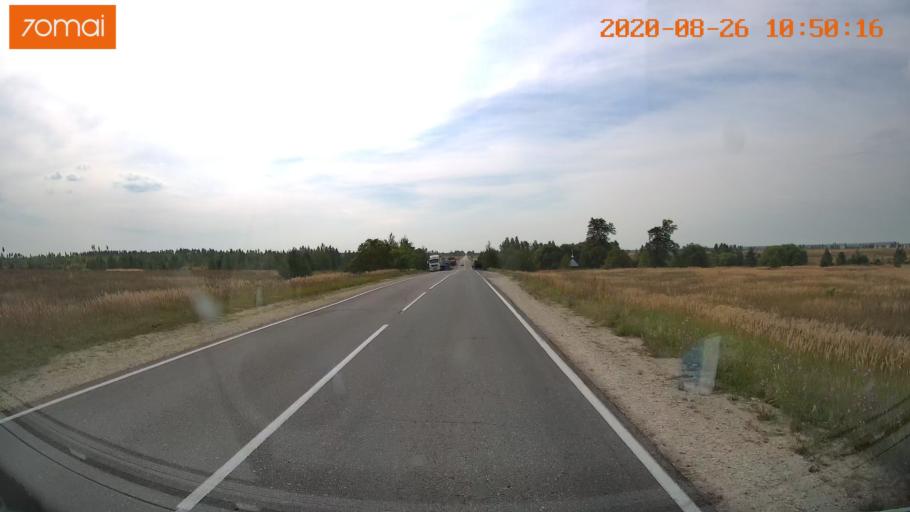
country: RU
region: Rjazan
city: Lashma
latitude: 54.6899
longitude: 41.1571
